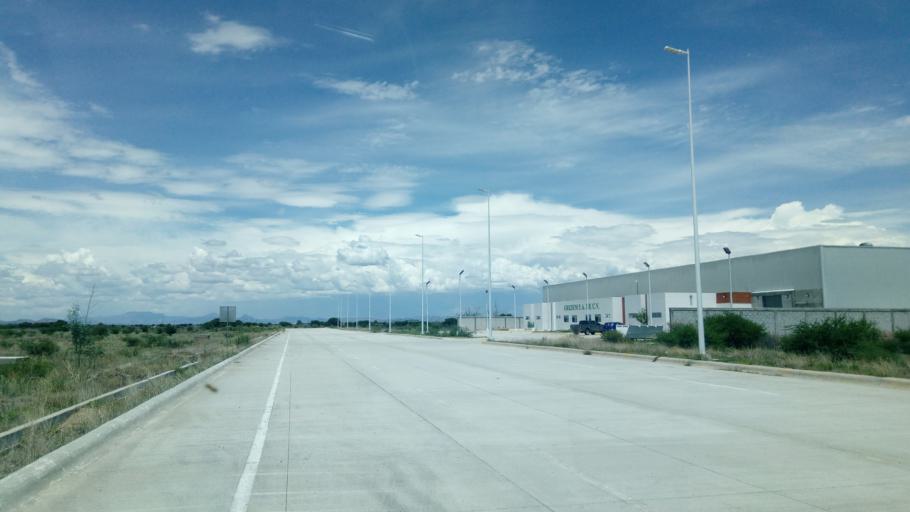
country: MX
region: Durango
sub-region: Durango
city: Jose Refugio Salcido
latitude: 24.1595
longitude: -104.5124
